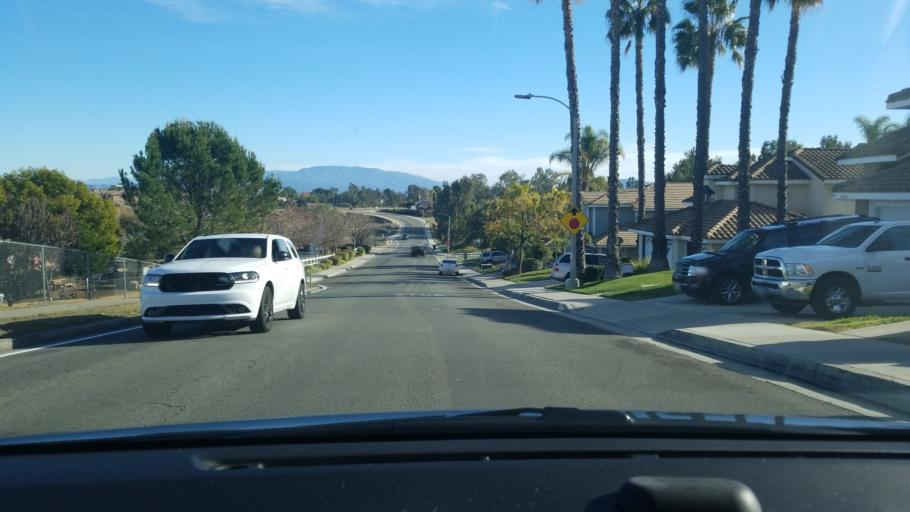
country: US
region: California
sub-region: Riverside County
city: Murrieta
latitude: 33.5681
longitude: -117.1946
